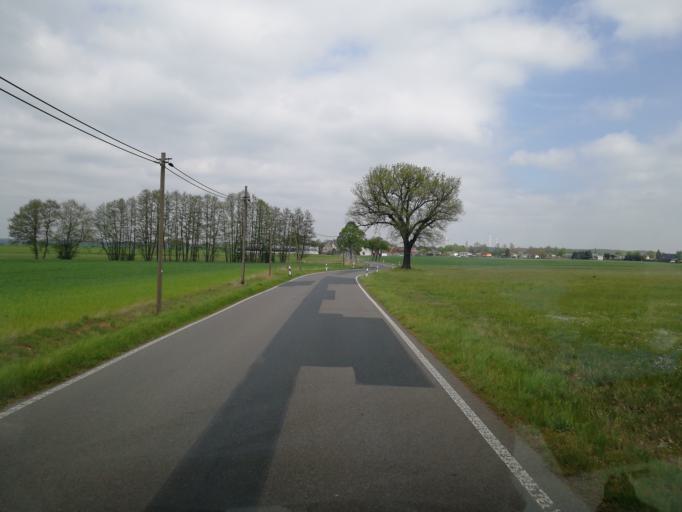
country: DE
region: Brandenburg
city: Hohenbucko
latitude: 51.6938
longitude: 13.4552
